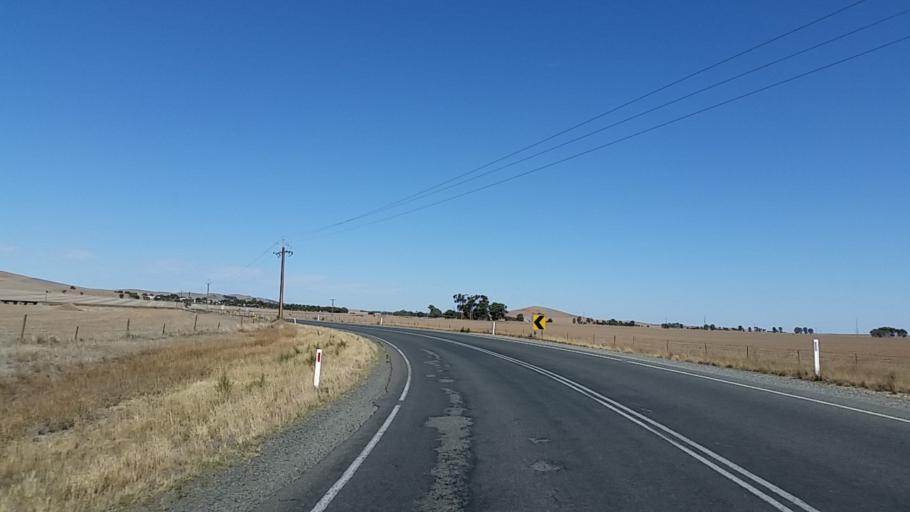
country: AU
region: South Australia
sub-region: Clare and Gilbert Valleys
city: Clare
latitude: -33.6840
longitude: 138.9058
